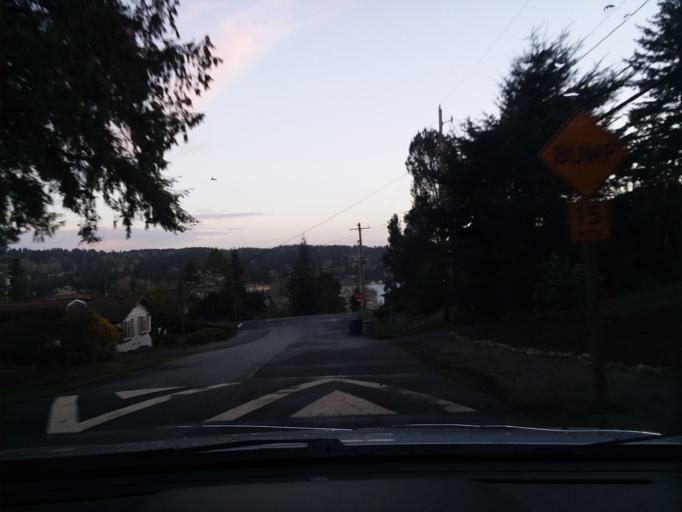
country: US
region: Washington
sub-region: King County
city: Kenmore
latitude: 47.7609
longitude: -122.2570
